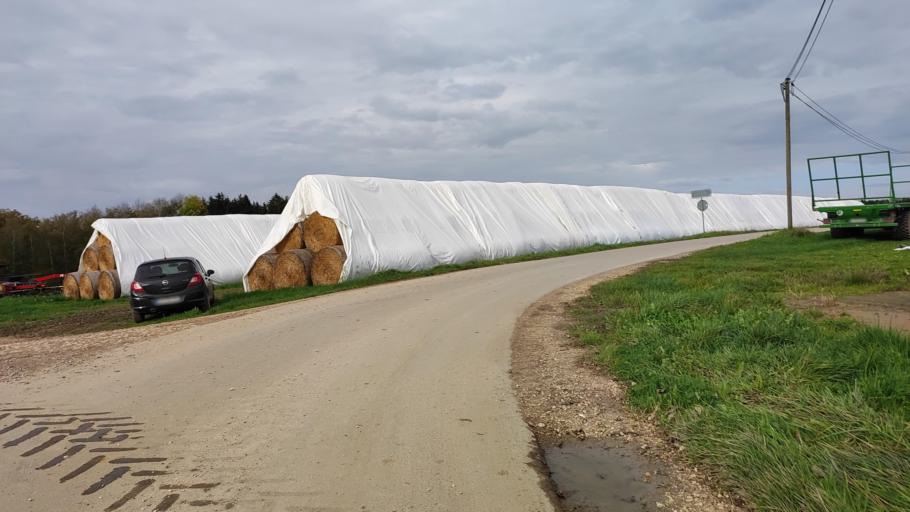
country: DE
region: Bavaria
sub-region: Swabia
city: Munsterhausen
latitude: 48.3164
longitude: 10.4812
